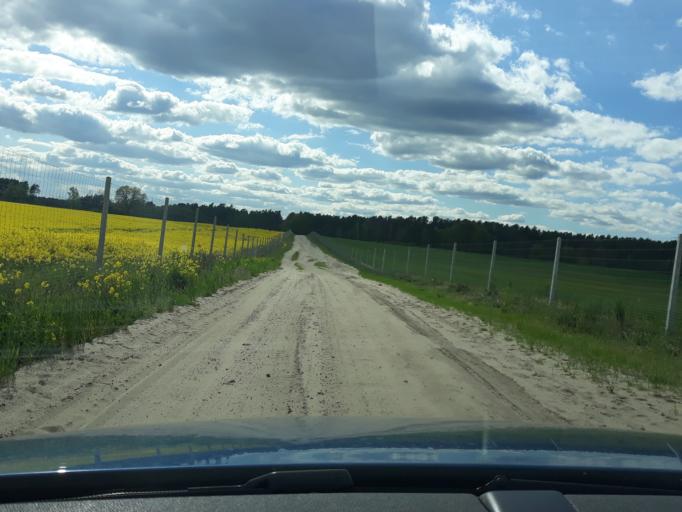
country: PL
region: Pomeranian Voivodeship
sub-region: Powiat czluchowski
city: Czluchow
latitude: 53.7194
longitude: 17.3544
